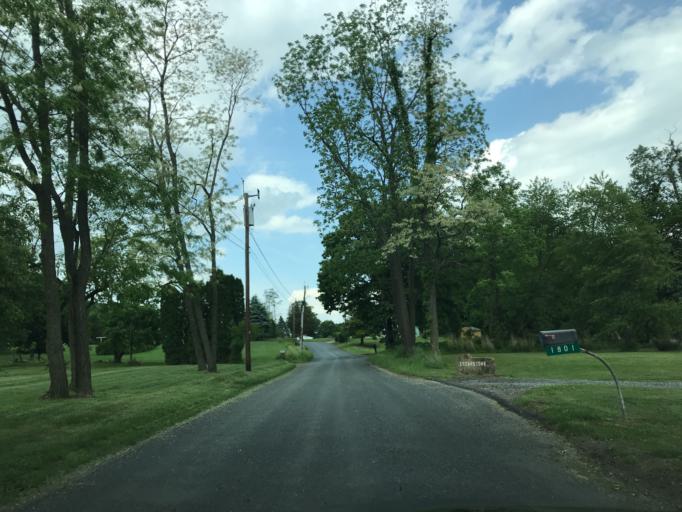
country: US
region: Pennsylvania
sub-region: York County
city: Susquehanna Trails
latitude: 39.7188
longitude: -76.3146
